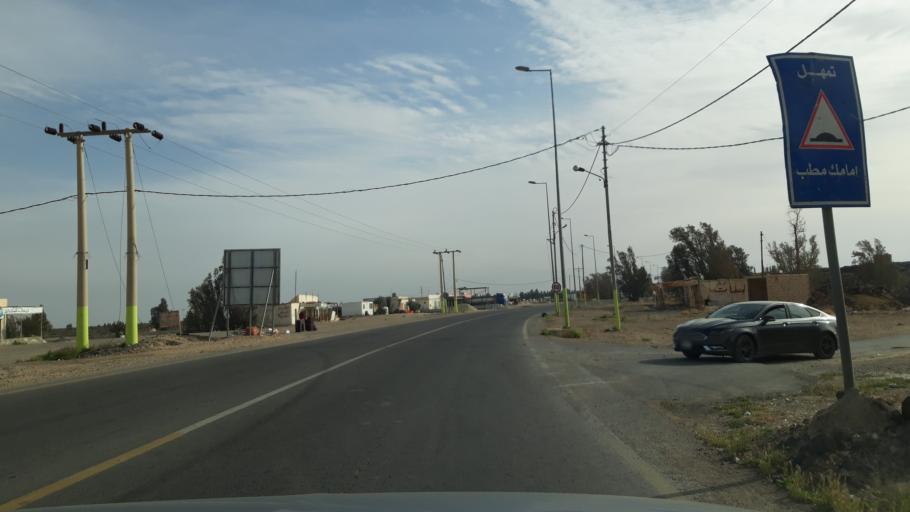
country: JO
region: Amman
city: Al Azraq ash Shamali
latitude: 31.8748
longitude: 36.8257
